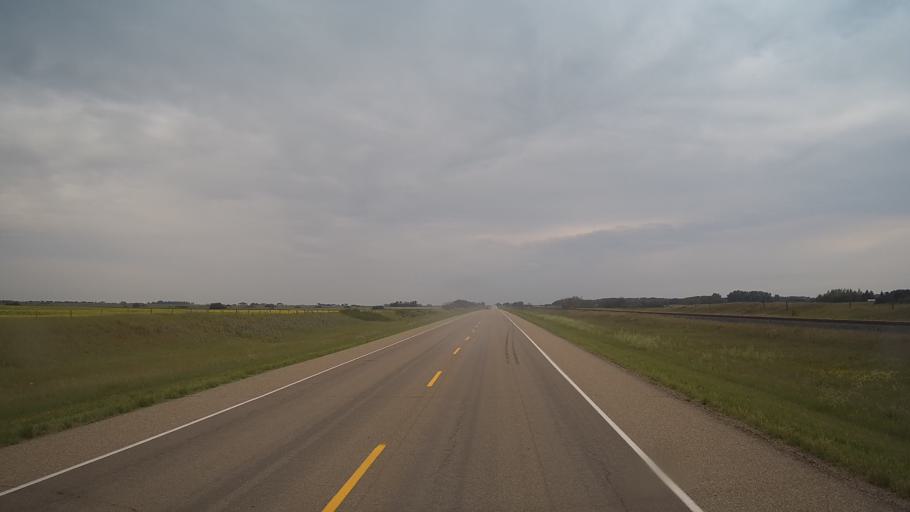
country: CA
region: Saskatchewan
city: Langham
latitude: 52.1274
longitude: -107.2562
